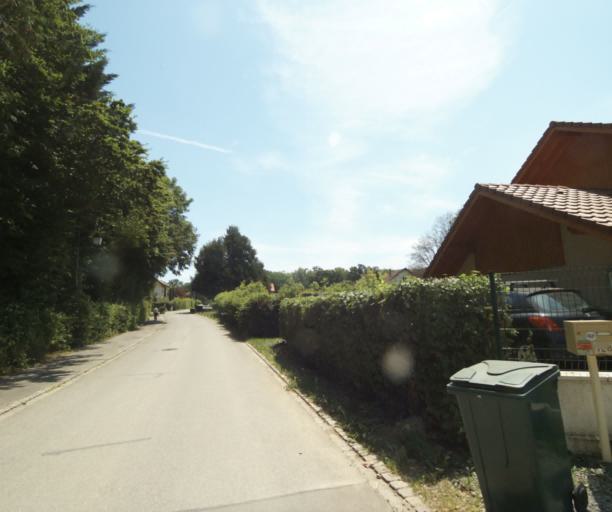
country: FR
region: Rhone-Alpes
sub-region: Departement de la Haute-Savoie
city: Messery
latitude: 46.3652
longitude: 6.3066
